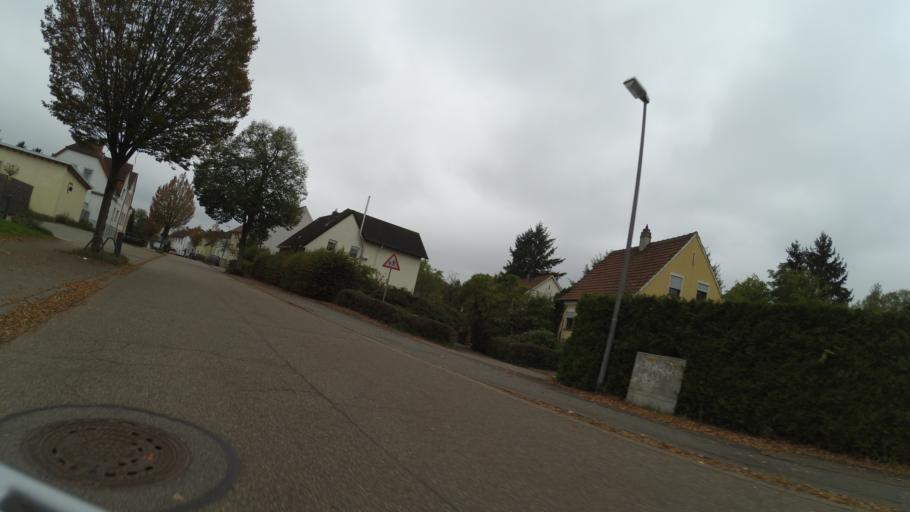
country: DE
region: Saarland
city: Homburg
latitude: 49.2955
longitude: 7.3188
